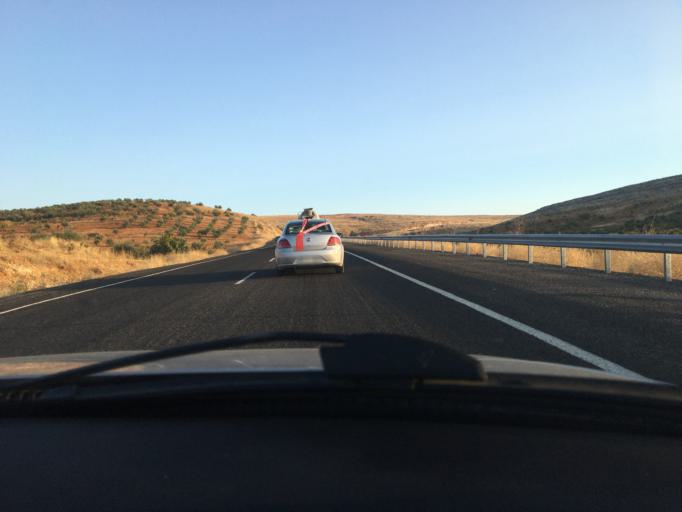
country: TR
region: Sanliurfa
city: Bogurtlen
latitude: 37.1895
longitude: 37.9711
